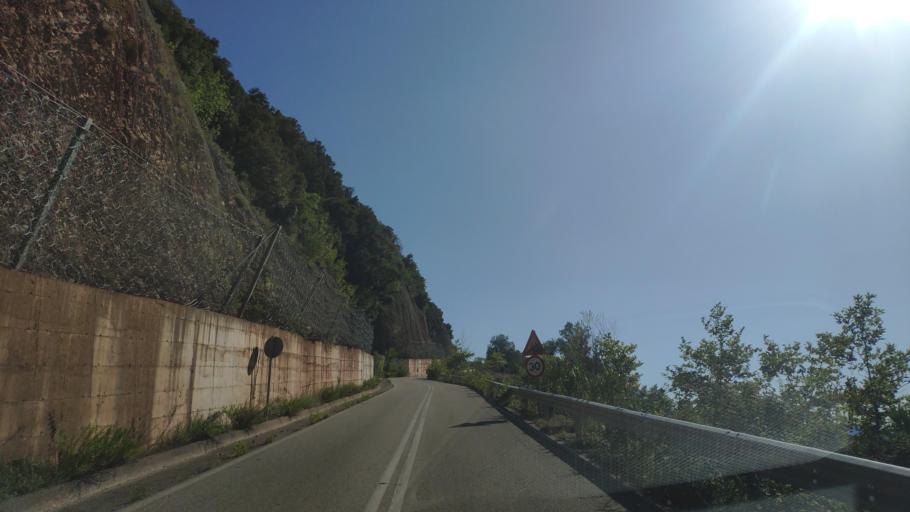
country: GR
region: Central Greece
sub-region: Nomos Evrytanias
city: Kerasochori
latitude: 39.0193
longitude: 21.6010
